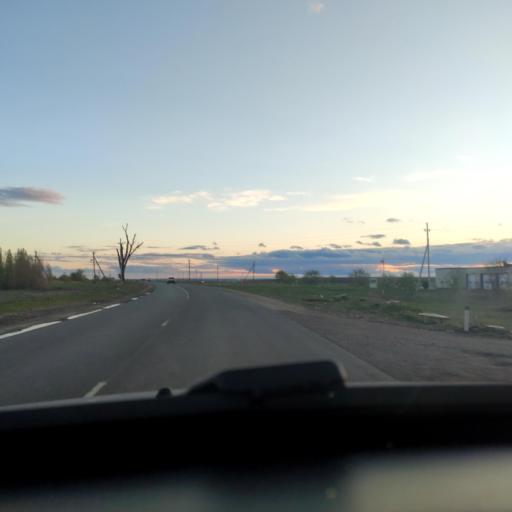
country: RU
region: Voronezj
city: Novovoronezh
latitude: 51.3470
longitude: 39.2864
